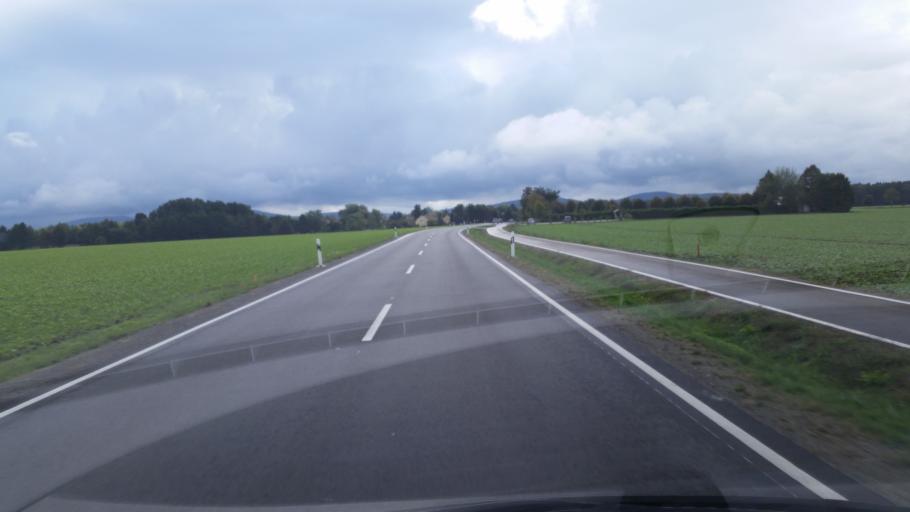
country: DE
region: Saxony
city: Kamenz
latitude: 51.3093
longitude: 14.1304
